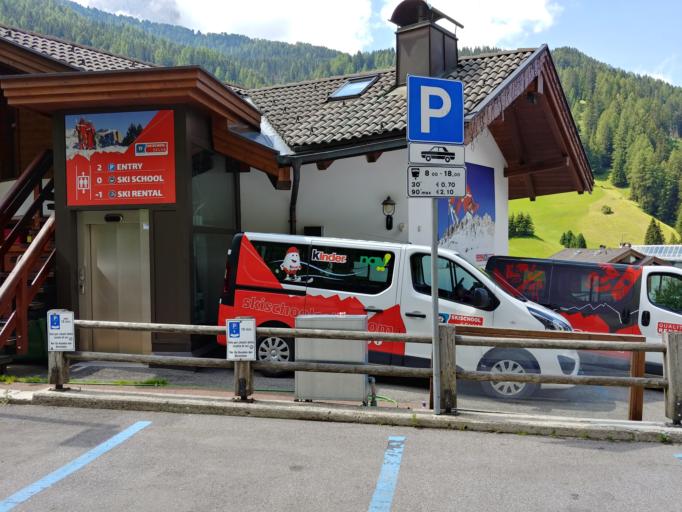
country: IT
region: Trentino-Alto Adige
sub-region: Bolzano
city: Selva
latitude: 46.5535
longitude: 11.7638
